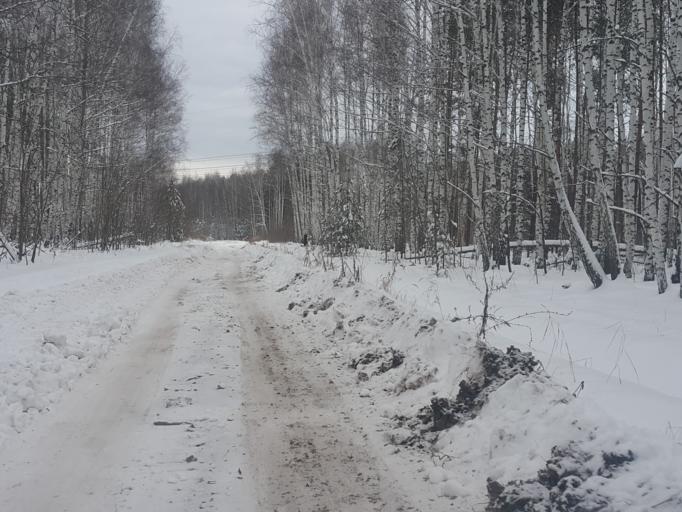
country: RU
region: Tambov
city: Platonovka
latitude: 52.8889
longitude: 41.8532
